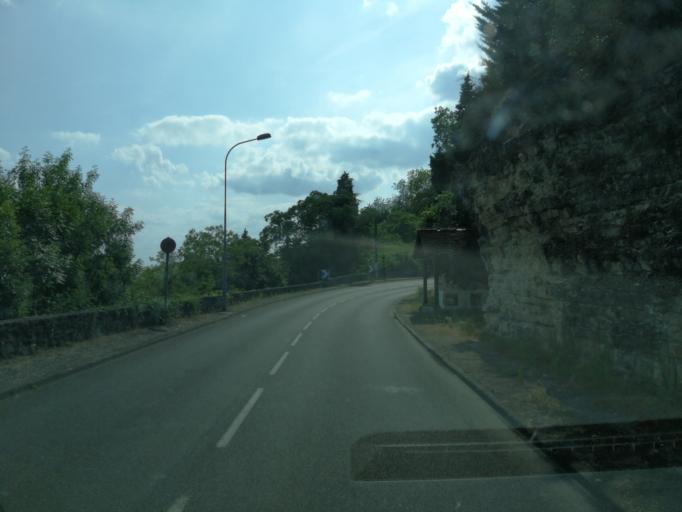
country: FR
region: Aquitaine
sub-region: Departement du Lot-et-Garonne
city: Fumel
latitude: 44.4975
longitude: 0.9732
